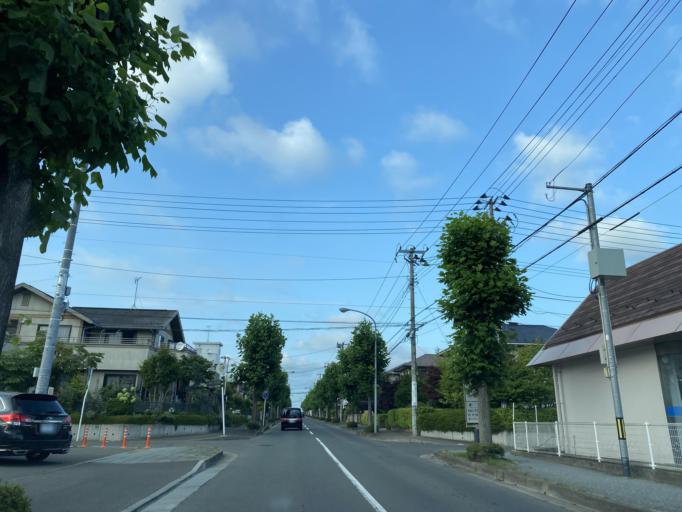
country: JP
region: Miyagi
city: Tomiya
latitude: 38.3802
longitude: 140.8644
